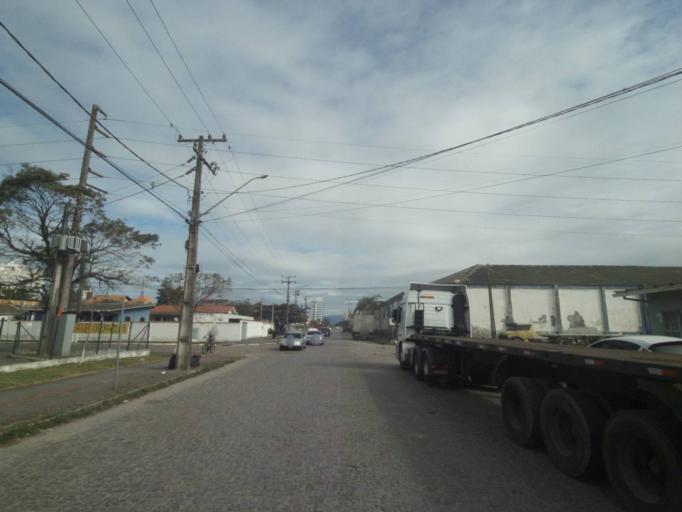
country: BR
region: Parana
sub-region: Paranagua
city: Paranagua
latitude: -25.5119
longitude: -48.5096
